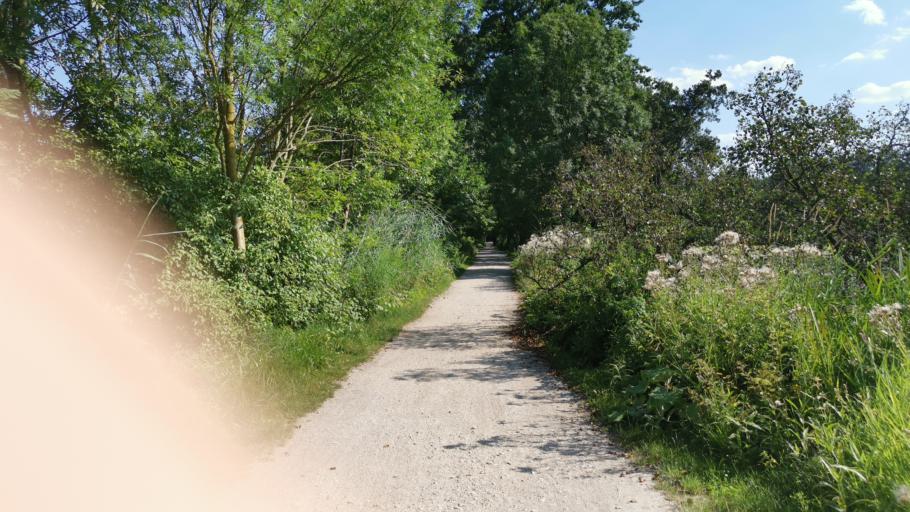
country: DE
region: Bavaria
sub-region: Regierungsbezirk Mittelfranken
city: Nuernberg
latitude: 49.4269
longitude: 11.1082
